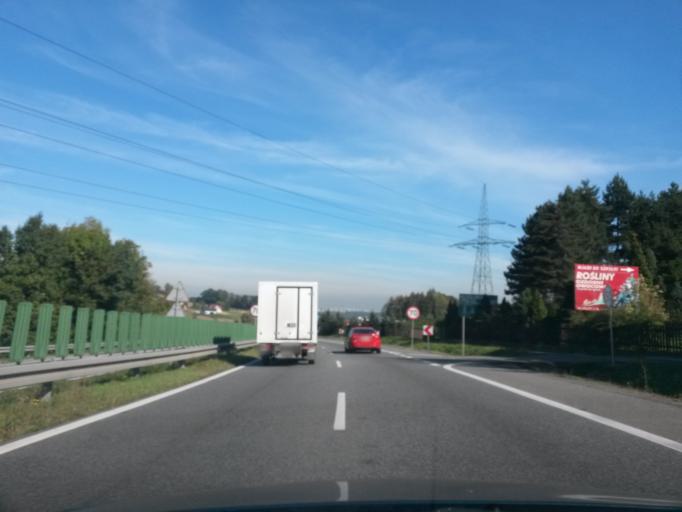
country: PL
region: Lesser Poland Voivodeship
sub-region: Powiat krakowski
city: Libertow
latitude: 49.9637
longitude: 19.8962
